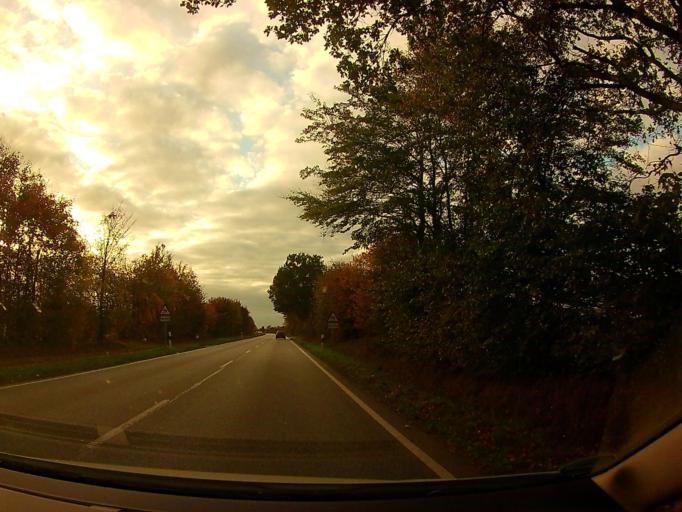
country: DE
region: Schleswig-Holstein
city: Schuby
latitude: 54.5188
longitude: 9.4619
